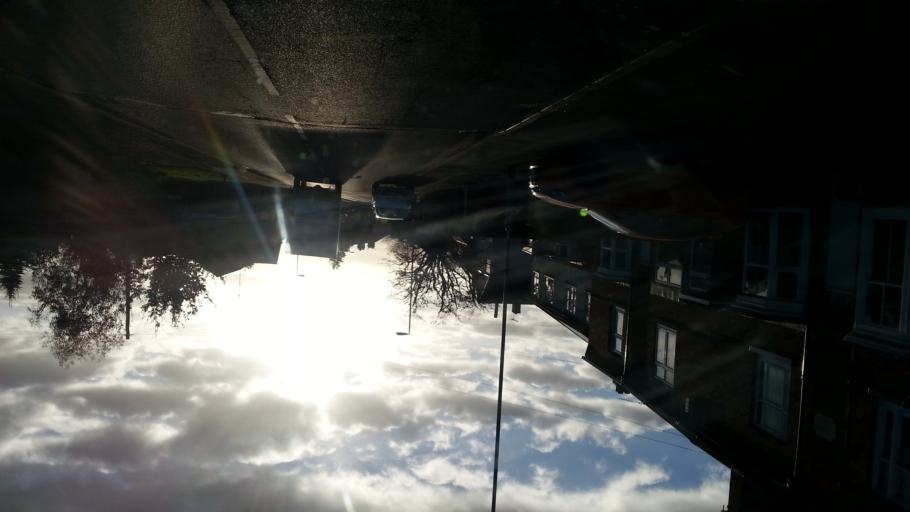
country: GB
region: England
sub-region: Leicestershire
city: Blaby
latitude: 52.5750
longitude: -1.1786
